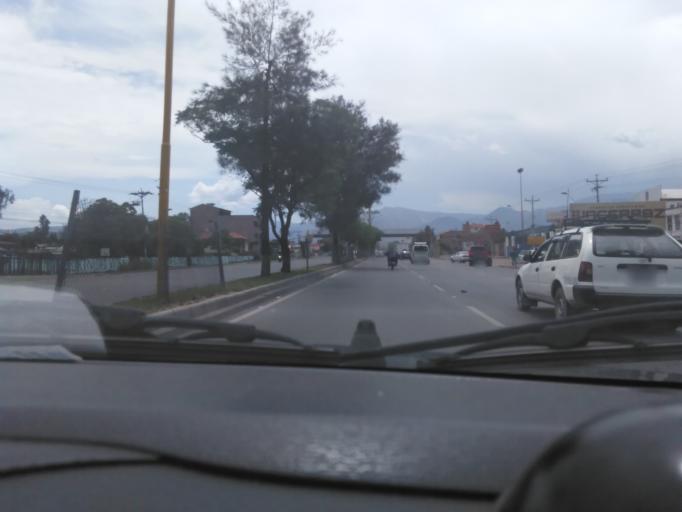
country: BO
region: Cochabamba
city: Cochabamba
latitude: -17.3916
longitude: -66.2562
